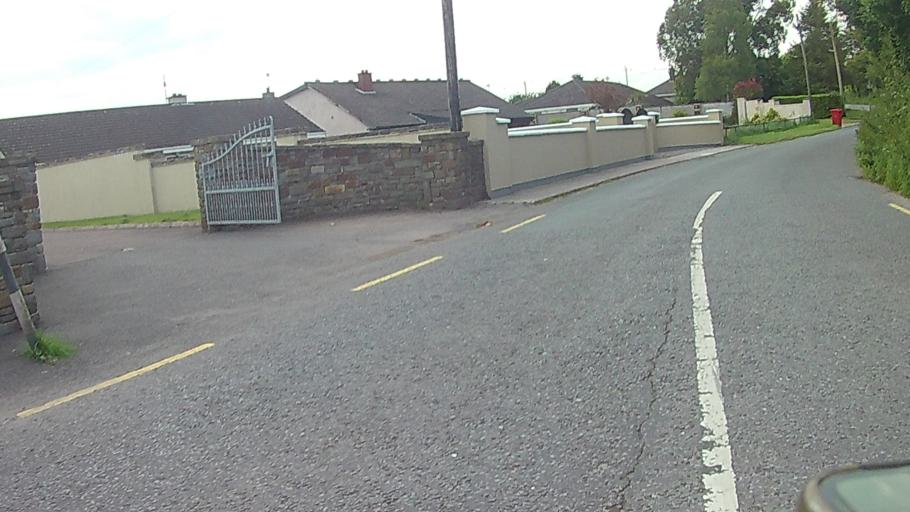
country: IE
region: Munster
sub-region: County Cork
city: Watergrasshill
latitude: 51.9640
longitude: -8.4087
